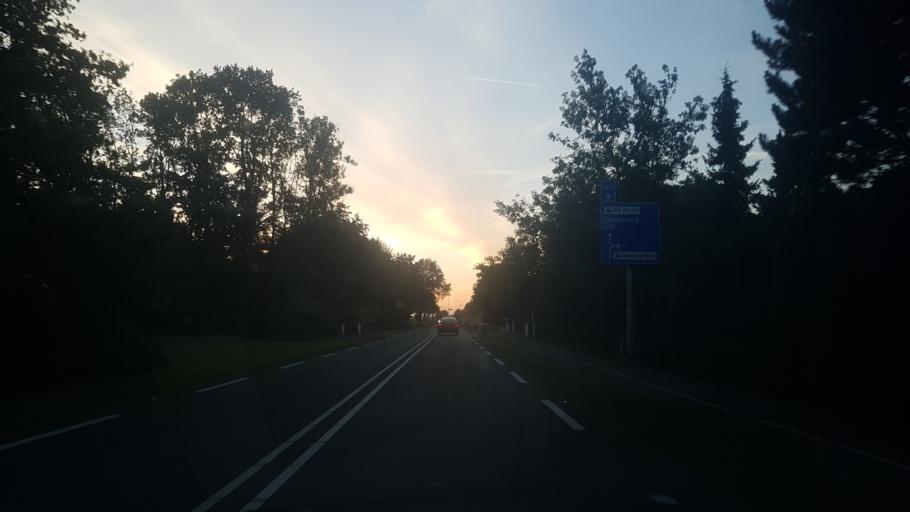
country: NL
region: Flevoland
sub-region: Gemeente Noordoostpolder
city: Emmeloord
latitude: 52.6871
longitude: 5.7376
